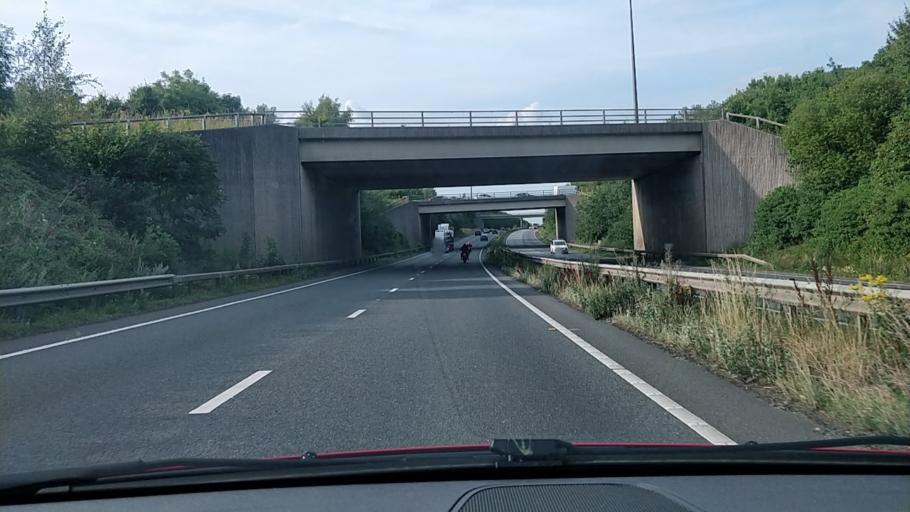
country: GB
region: England
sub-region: Cheshire West and Chester
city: Guilden Sutton
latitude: 53.1942
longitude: -2.8447
